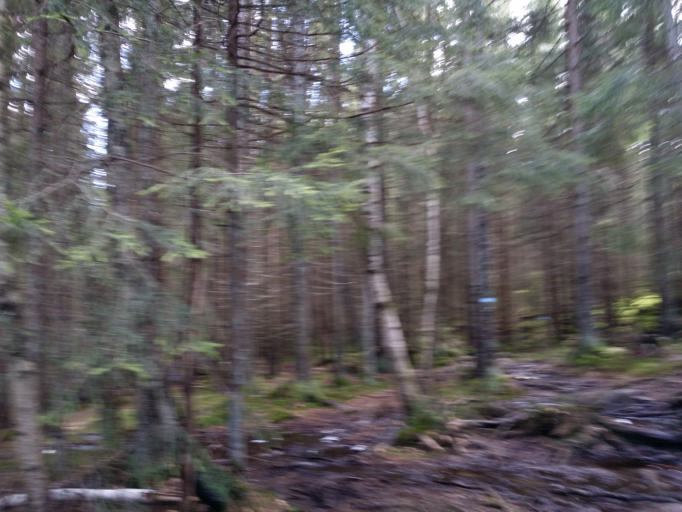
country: NO
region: Oslo
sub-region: Oslo
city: Sjolyststranda
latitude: 59.9883
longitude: 10.7069
